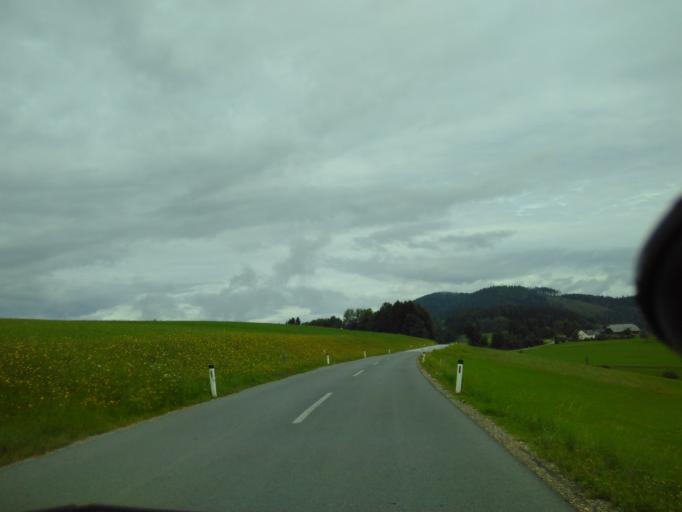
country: AT
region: Styria
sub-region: Politischer Bezirk Graz-Umgebung
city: Semriach
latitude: 47.2643
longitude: 15.4163
